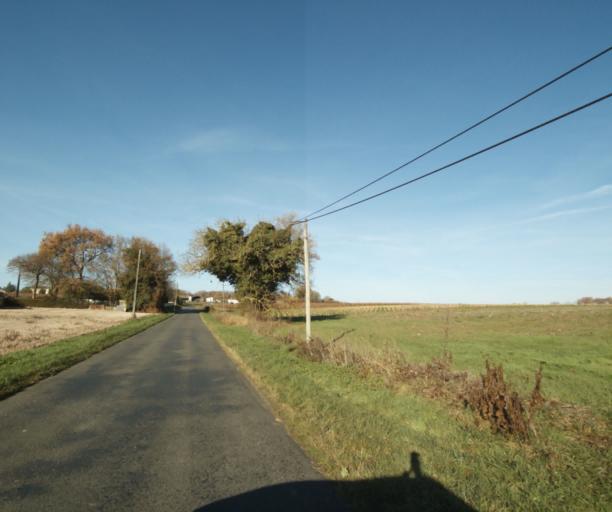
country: FR
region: Poitou-Charentes
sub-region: Departement de la Charente-Maritime
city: Cherac
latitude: 45.7075
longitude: -0.4463
